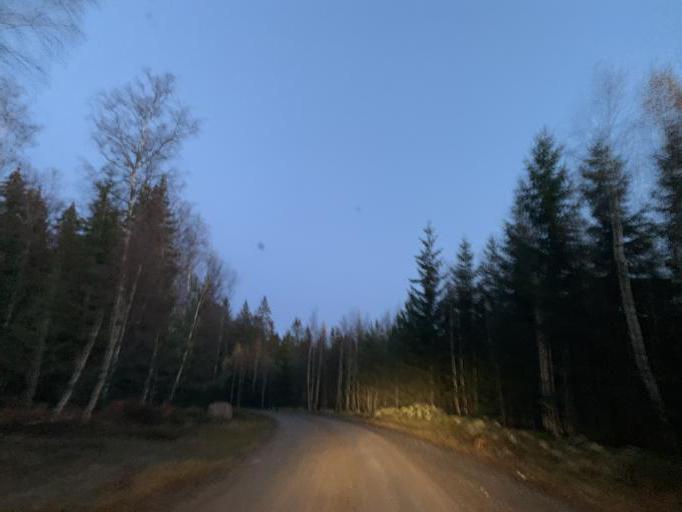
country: SE
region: OErebro
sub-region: Lindesbergs Kommun
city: Fellingsbro
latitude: 59.3752
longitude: 15.6126
